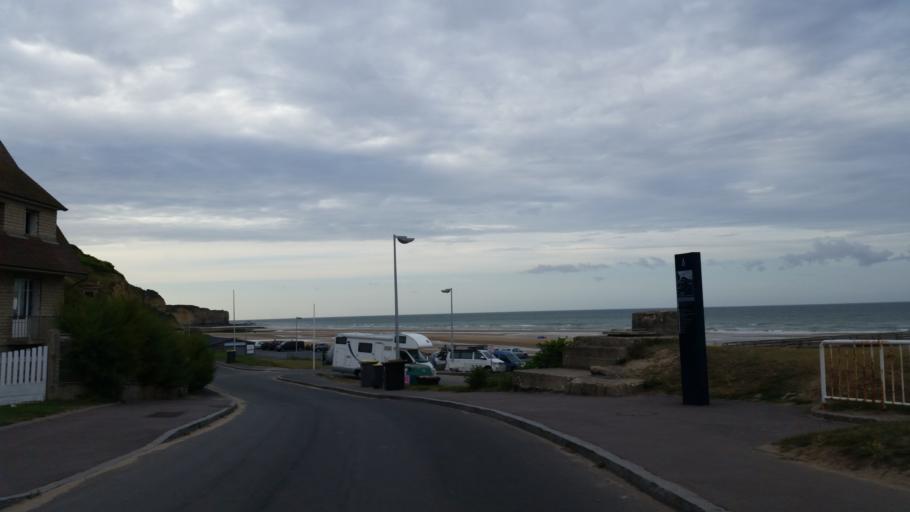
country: FR
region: Lower Normandy
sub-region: Departement du Calvados
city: Grandcamp-Maisy
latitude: 49.3794
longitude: -0.9035
